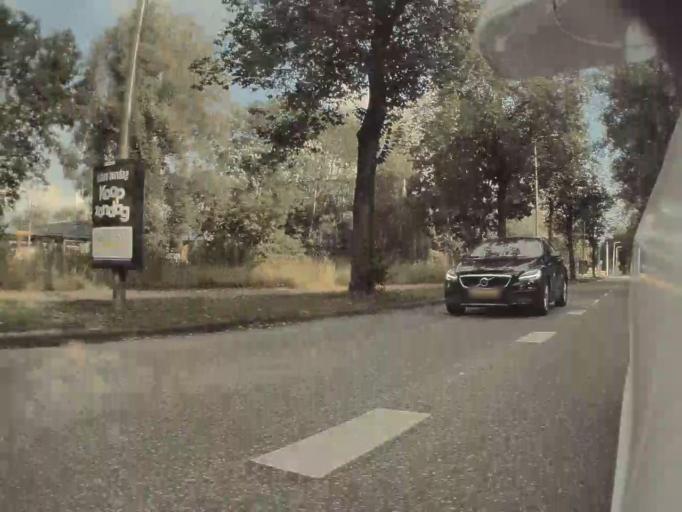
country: NL
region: Utrecht
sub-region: Gemeente Utrecht
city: Utrecht
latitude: 52.1127
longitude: 5.1076
